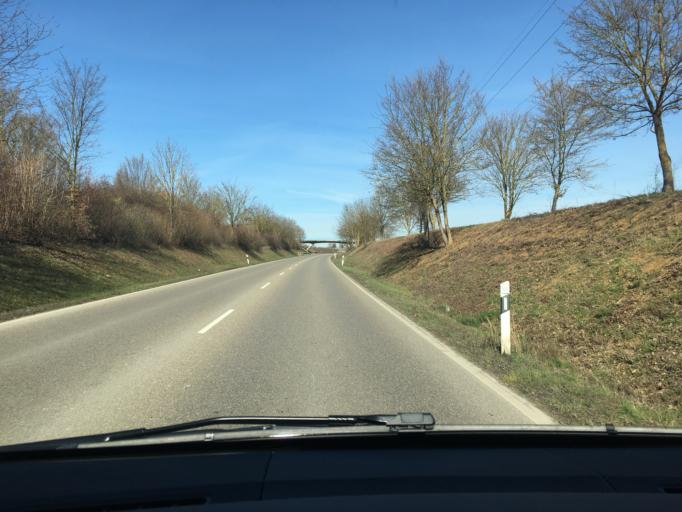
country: DE
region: Baden-Wuerttemberg
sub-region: Regierungsbezirk Stuttgart
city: Denkendorf
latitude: 48.7161
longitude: 9.3061
